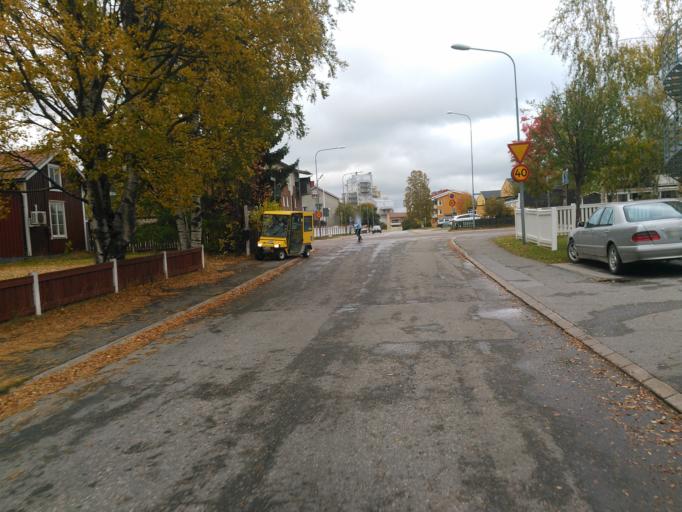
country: SE
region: Vaesterbotten
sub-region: Umea Kommun
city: Umea
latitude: 63.8204
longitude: 20.2468
